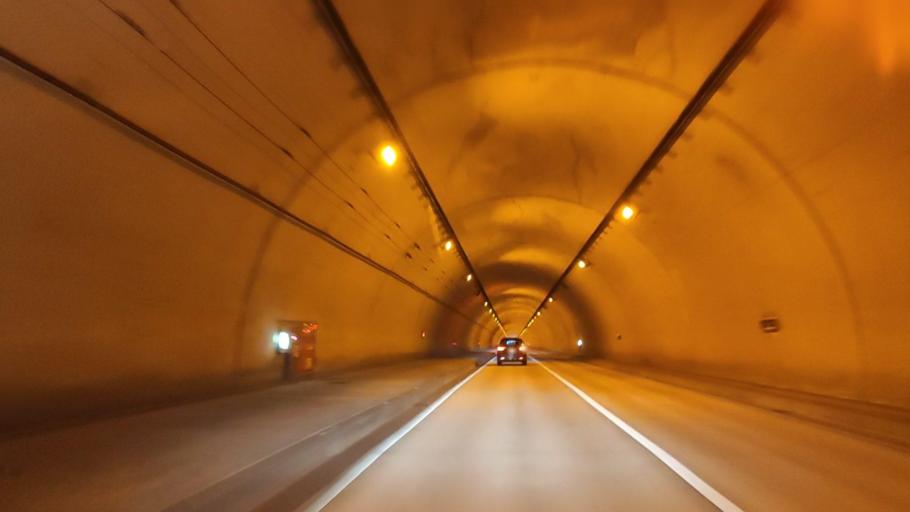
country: JP
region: Ehime
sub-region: Shikoku-chuo Shi
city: Matsuyama
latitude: 33.8825
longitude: 132.7101
